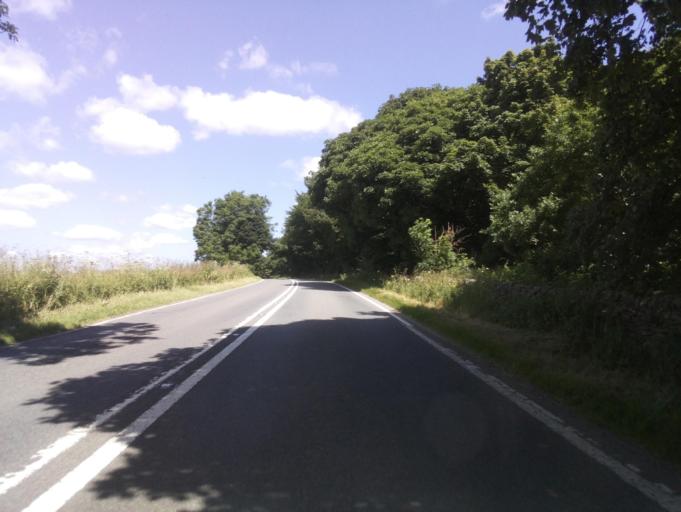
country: GB
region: England
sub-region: Derbyshire
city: Ashbourne
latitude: 53.1110
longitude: -1.7562
